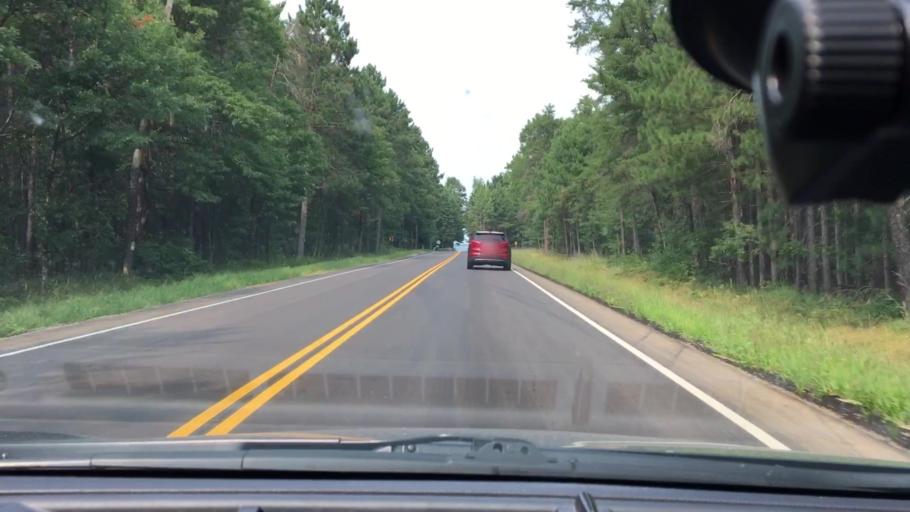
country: US
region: Minnesota
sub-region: Crow Wing County
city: Breezy Point
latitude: 46.5319
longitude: -94.1824
